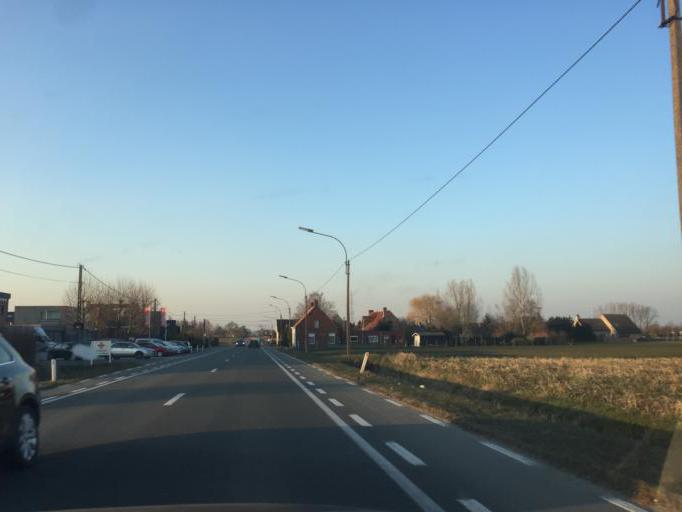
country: BE
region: Flanders
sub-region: Provincie West-Vlaanderen
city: Pittem
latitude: 50.9687
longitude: 3.2431
